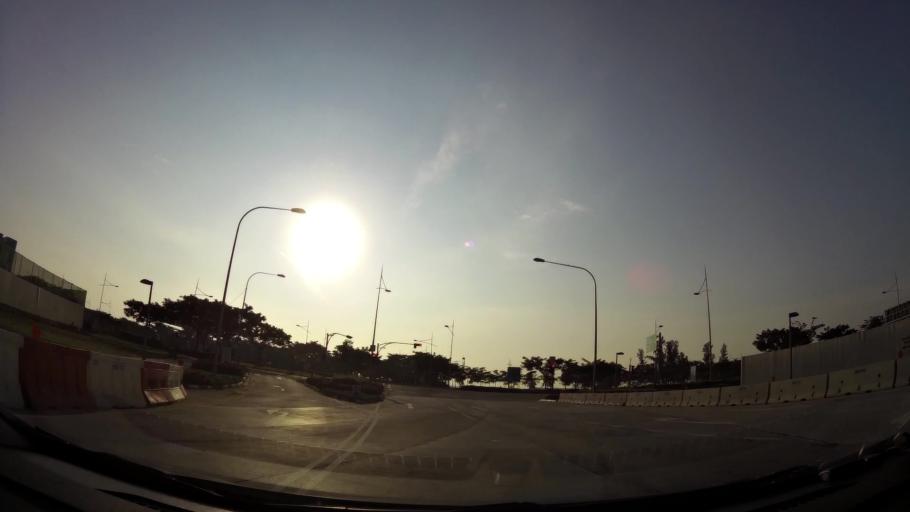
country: SG
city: Singapore
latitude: 1.2741
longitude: 103.8644
